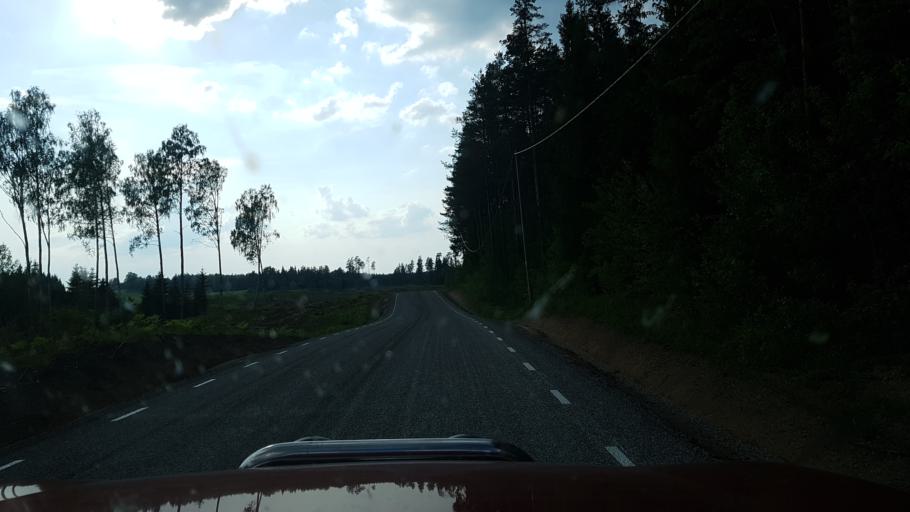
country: EE
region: Tartu
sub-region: UElenurme vald
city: Ulenurme
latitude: 58.1086
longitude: 26.7474
